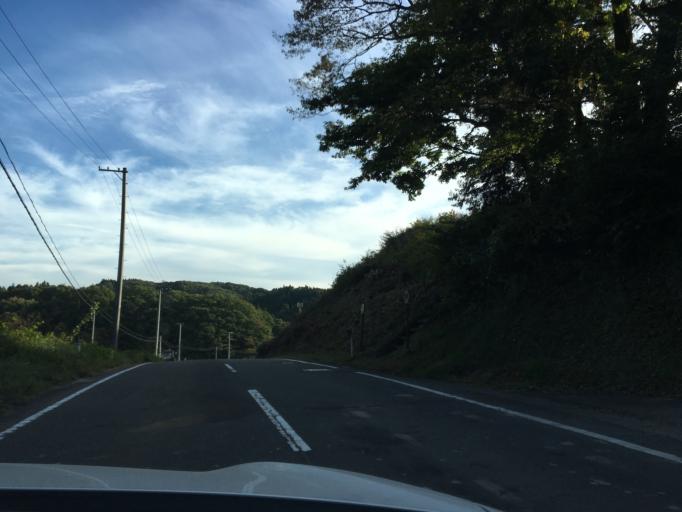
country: JP
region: Fukushima
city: Ishikawa
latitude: 37.2088
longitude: 140.5960
